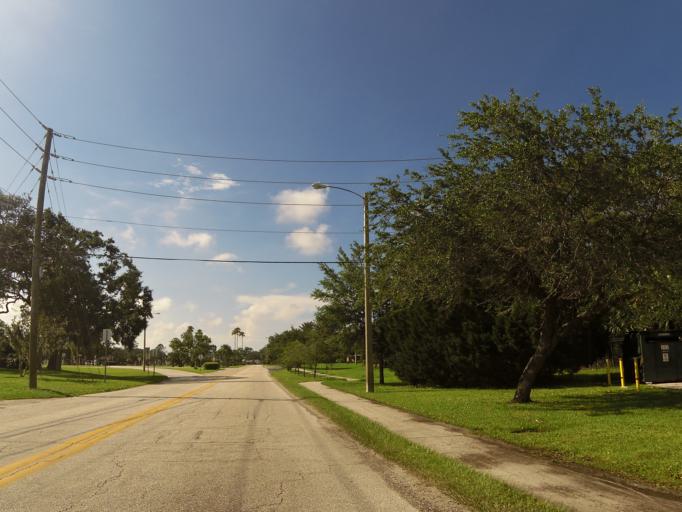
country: US
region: Florida
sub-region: Saint Johns County
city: Villano Beach
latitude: 29.9215
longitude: -81.3241
